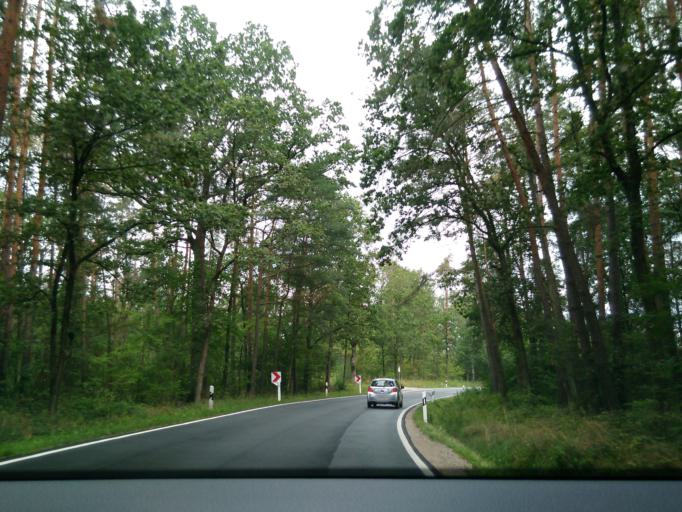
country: DE
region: Bavaria
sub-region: Regierungsbezirk Mittelfranken
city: Weisendorf
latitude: 49.6528
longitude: 10.8091
